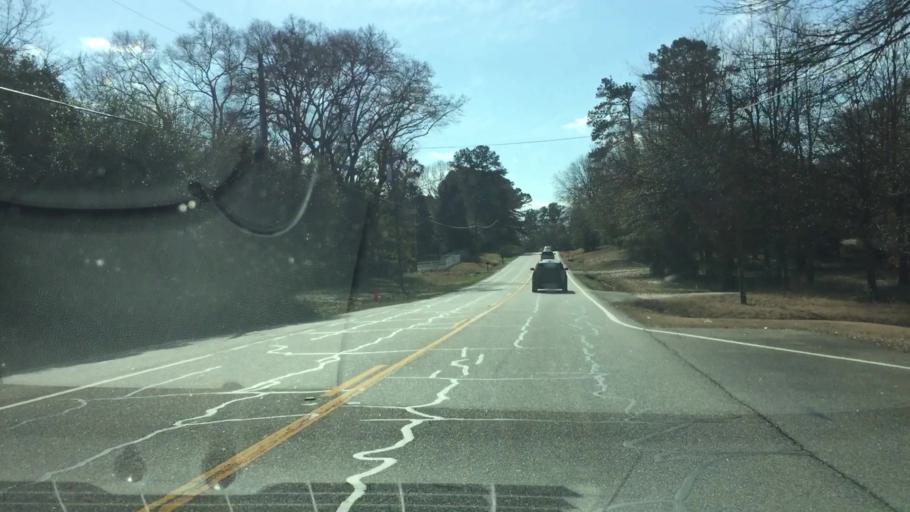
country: US
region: Georgia
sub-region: Henry County
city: McDonough
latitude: 33.4659
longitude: -84.1408
